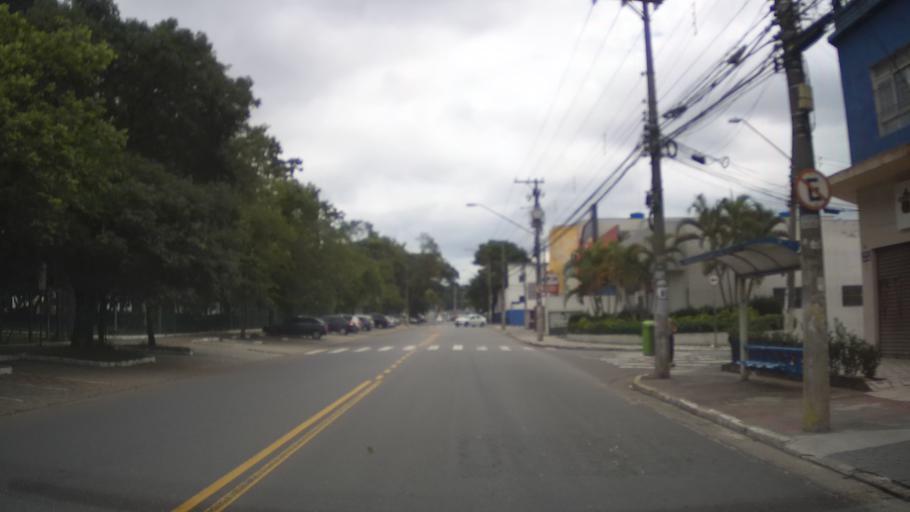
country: BR
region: Sao Paulo
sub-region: Guarulhos
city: Guarulhos
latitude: -23.4548
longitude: -46.5169
